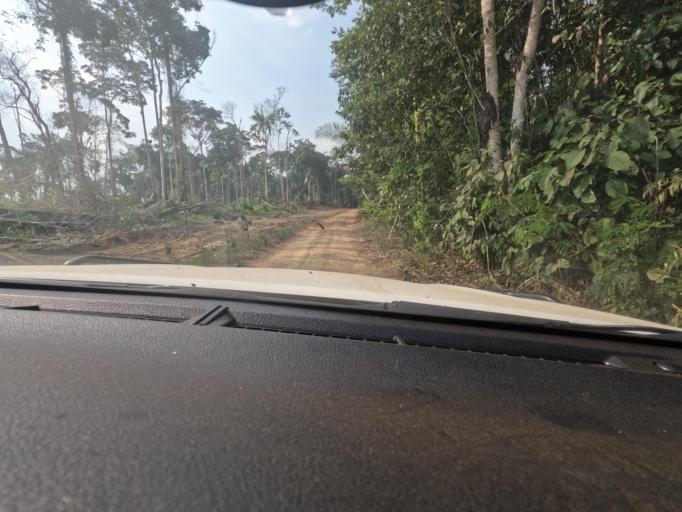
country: BR
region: Rondonia
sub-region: Porto Velho
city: Porto Velho
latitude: -8.6690
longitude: -63.1558
